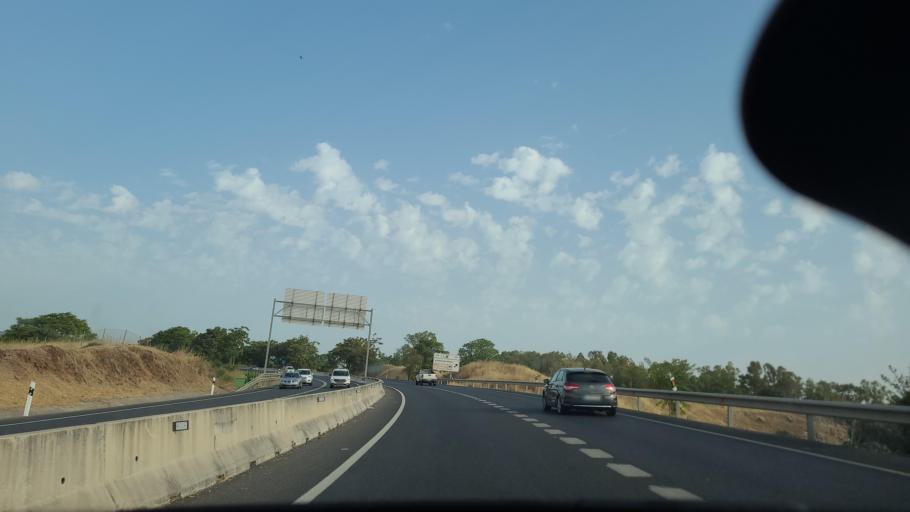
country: ES
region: Andalusia
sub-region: Province of Cordoba
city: Cordoba
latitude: 37.9120
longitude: -4.7530
